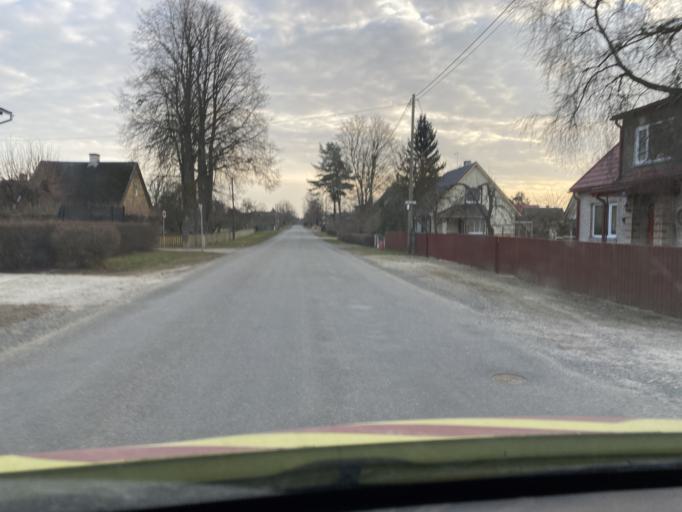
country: EE
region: Jogevamaa
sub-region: Poltsamaa linn
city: Poltsamaa
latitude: 58.6508
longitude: 25.9635
